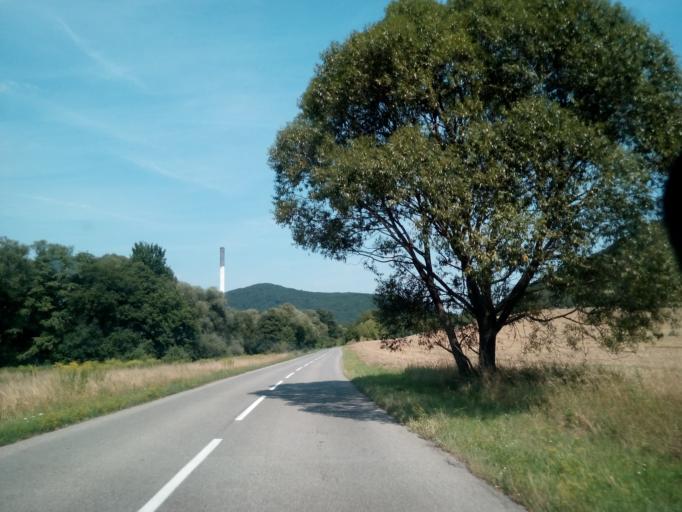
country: SK
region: Kosicky
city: Kosice
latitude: 48.8480
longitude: 21.2269
